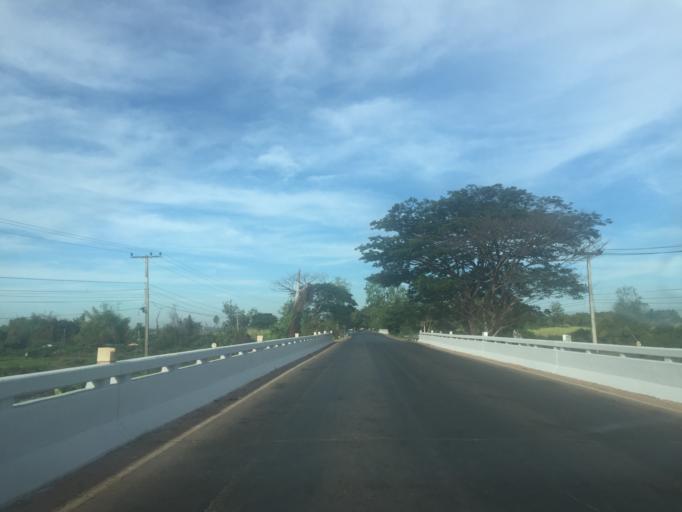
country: TH
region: Kalasin
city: Tha Khantho
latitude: 16.9621
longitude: 103.2543
